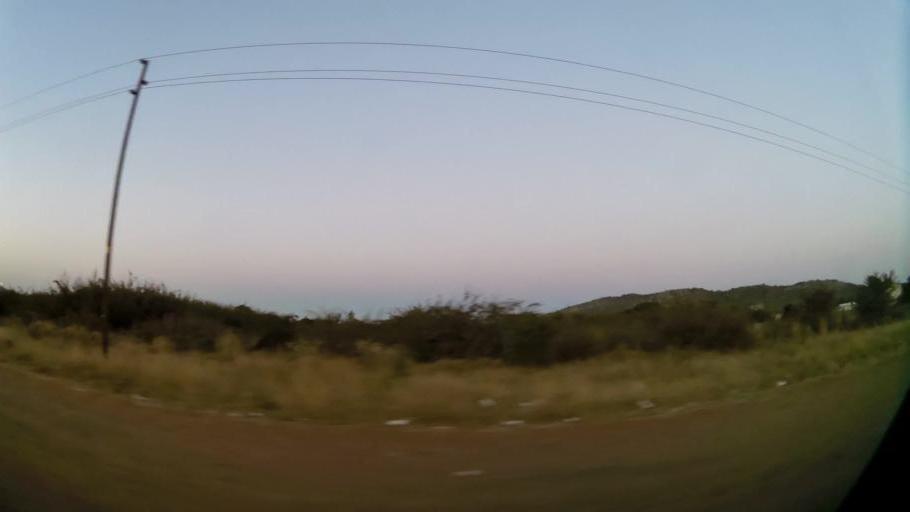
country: ZA
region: North-West
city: Ga-Rankuwa
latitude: -25.6260
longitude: 27.9628
